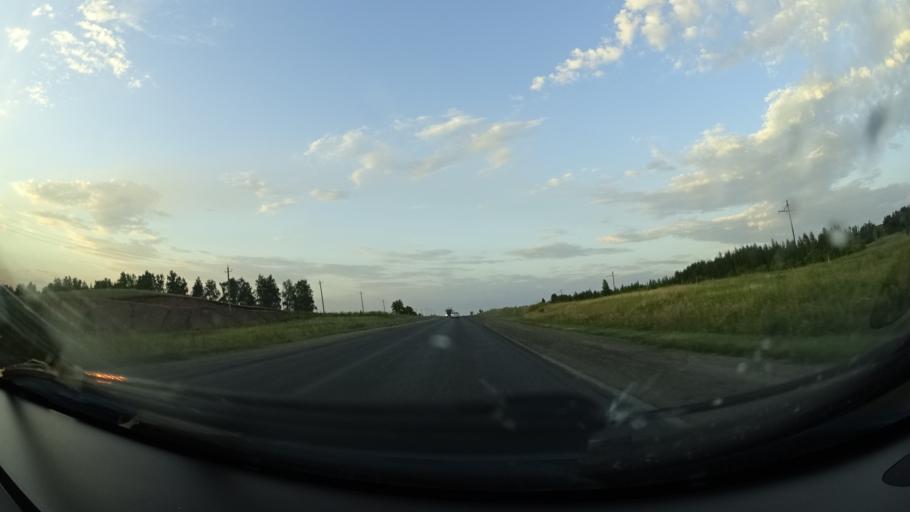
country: RU
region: Orenburg
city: Severnoye
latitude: 54.1847
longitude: 52.6648
